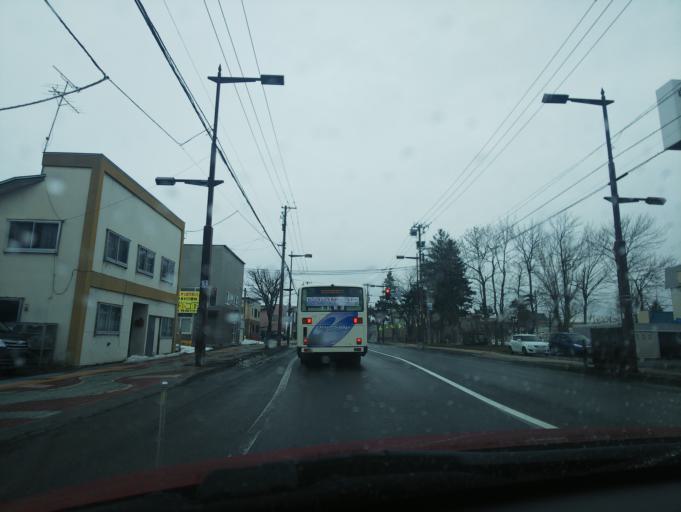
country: JP
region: Hokkaido
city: Nayoro
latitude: 44.1704
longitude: 142.3939
